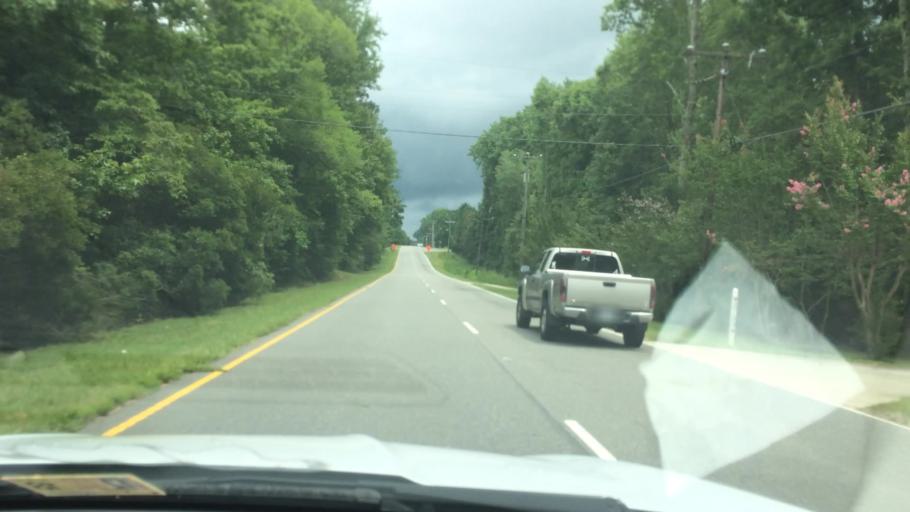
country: US
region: Virginia
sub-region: King William County
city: West Point
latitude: 37.4035
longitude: -76.8302
